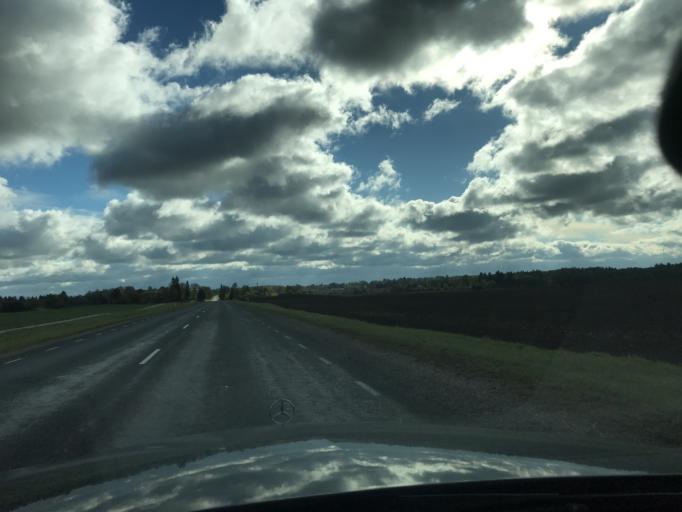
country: EE
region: Vorumaa
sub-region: Antsla vald
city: Vana-Antsla
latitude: 57.9521
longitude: 26.2839
